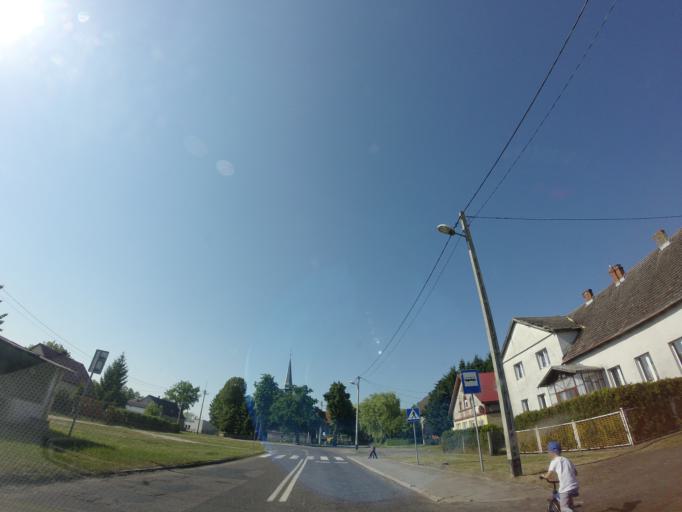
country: PL
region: West Pomeranian Voivodeship
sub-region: Powiat stargardzki
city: Kobylanka
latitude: 53.3234
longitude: 14.8564
